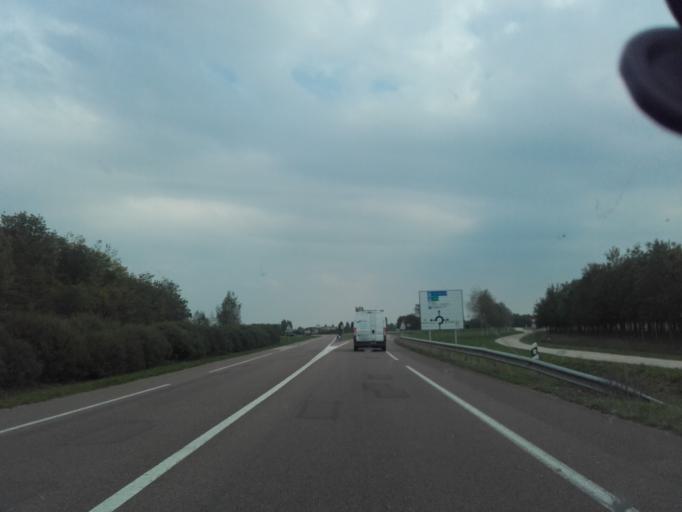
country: FR
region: Bourgogne
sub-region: Departement de la Cote-d'Or
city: Bligny-les-Beaune
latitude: 47.0071
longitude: 4.8233
